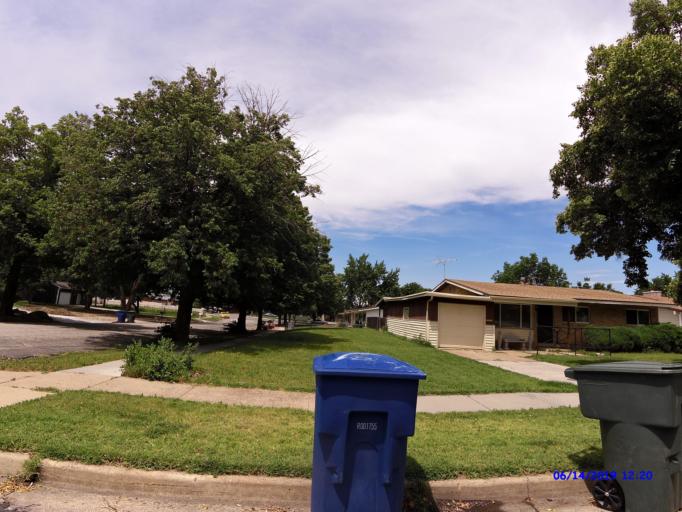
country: US
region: Utah
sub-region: Weber County
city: Ogden
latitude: 41.2526
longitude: -111.9503
